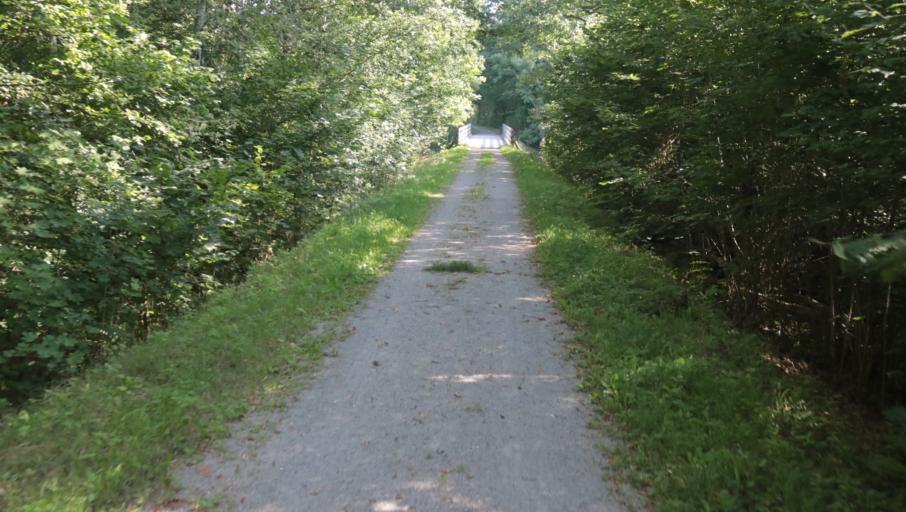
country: SE
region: Blekinge
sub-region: Karlshamns Kommun
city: Svangsta
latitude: 56.3763
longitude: 14.6805
